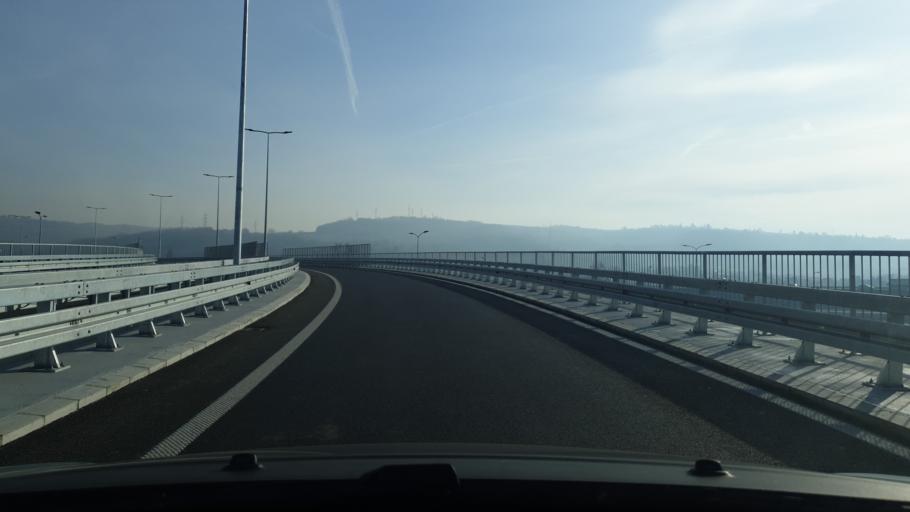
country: RS
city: Baric
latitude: 44.6522
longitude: 20.2310
